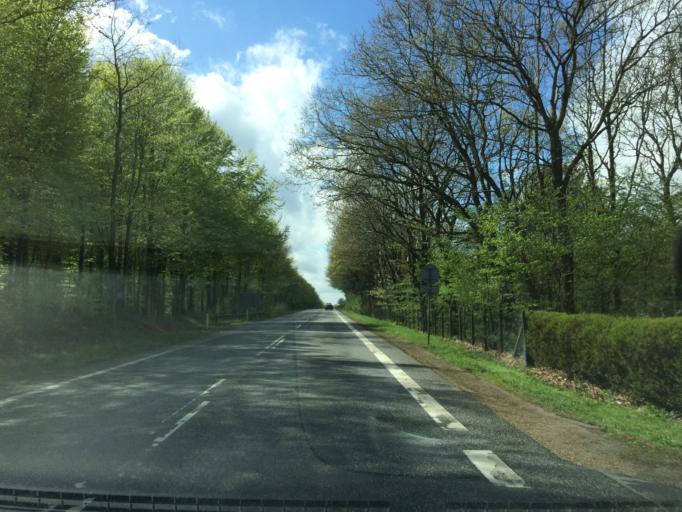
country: DK
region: Central Jutland
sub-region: Viborg Kommune
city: Stoholm
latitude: 56.4261
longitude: 9.0814
